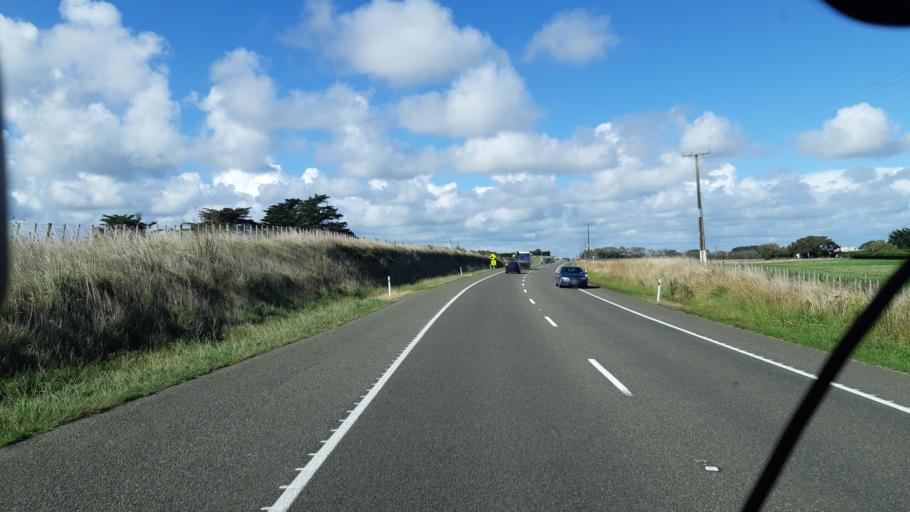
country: NZ
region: Manawatu-Wanganui
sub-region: Wanganui District
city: Wanganui
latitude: -39.9752
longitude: 175.1286
